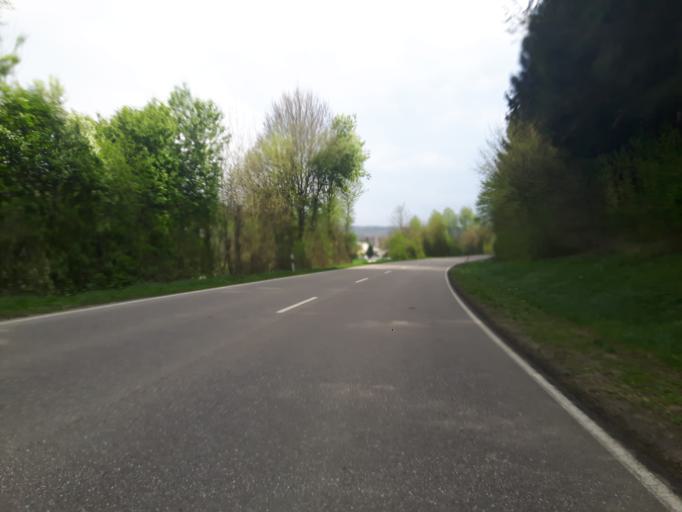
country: DE
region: Baden-Wuerttemberg
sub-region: Regierungsbezirk Stuttgart
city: Jagsthausen
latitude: 49.2814
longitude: 9.4674
